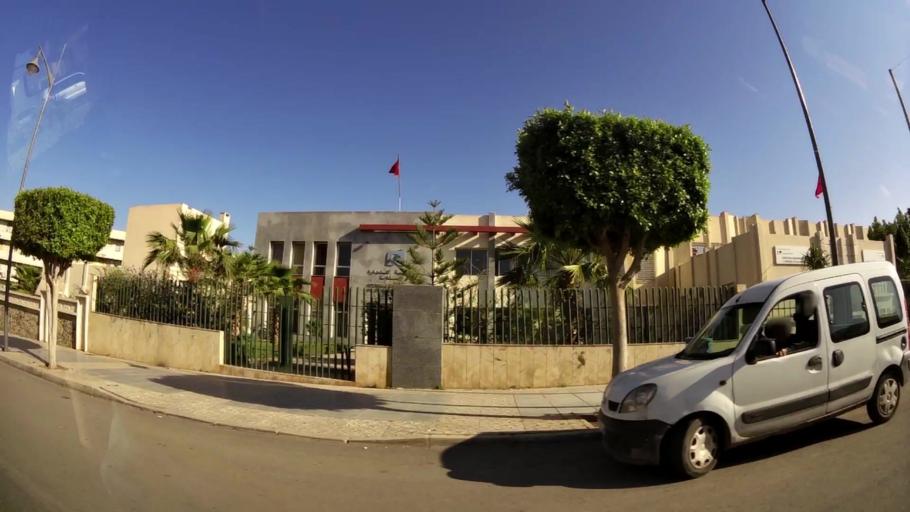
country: MA
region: Oriental
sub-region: Oujda-Angad
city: Oujda
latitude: 34.6914
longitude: -1.9106
